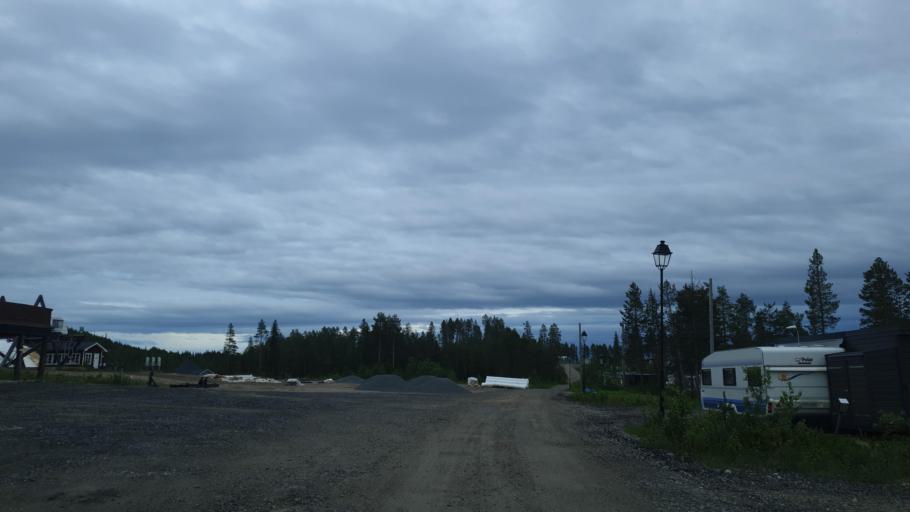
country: SE
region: Norrbotten
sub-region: Jokkmokks Kommun
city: Jokkmokk
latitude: 66.1553
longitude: 19.9885
